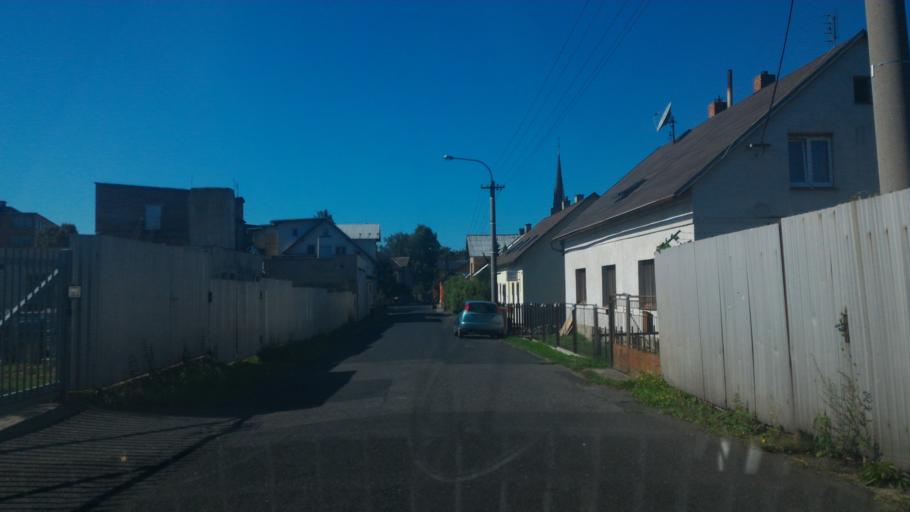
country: CZ
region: Ustecky
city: Varnsdorf
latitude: 50.9132
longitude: 14.6322
